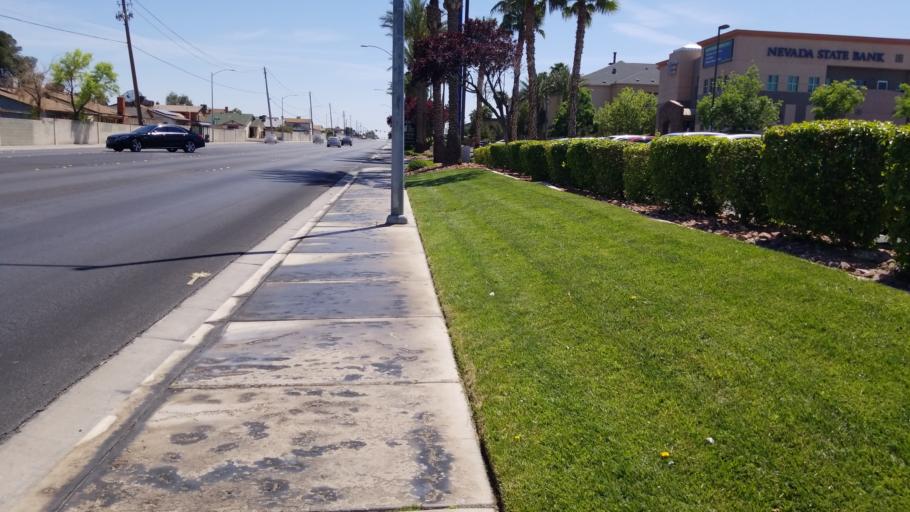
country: US
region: Nevada
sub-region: Clark County
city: Spring Valley
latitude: 36.1939
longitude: -115.2424
